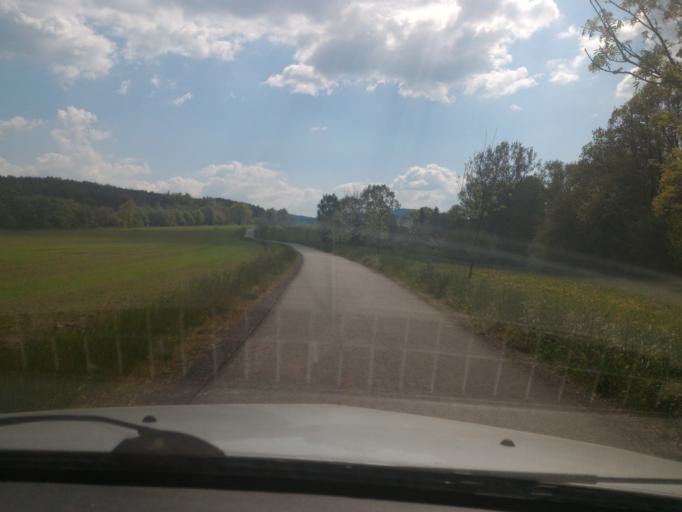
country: DE
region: Saxony
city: Olbersdorf
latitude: 50.8959
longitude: 14.7573
